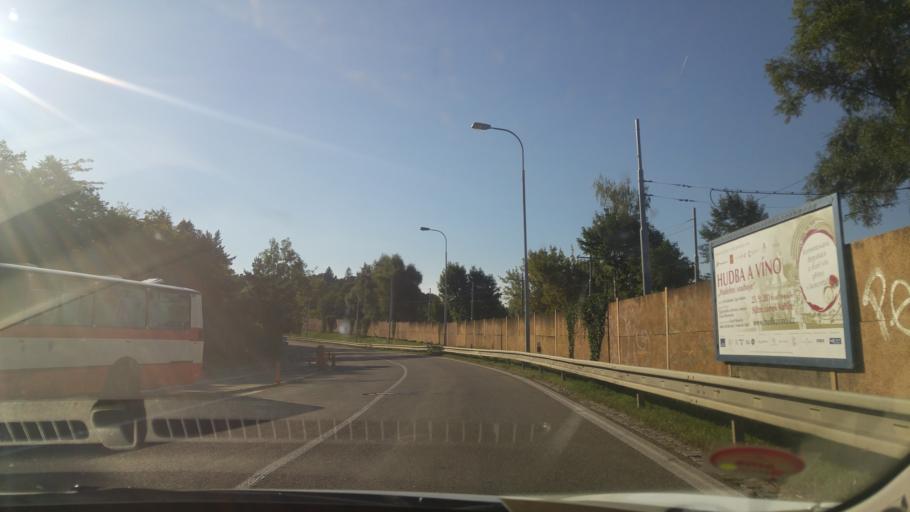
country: CZ
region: South Moravian
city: Troubsko
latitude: 49.2288
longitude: 16.5304
